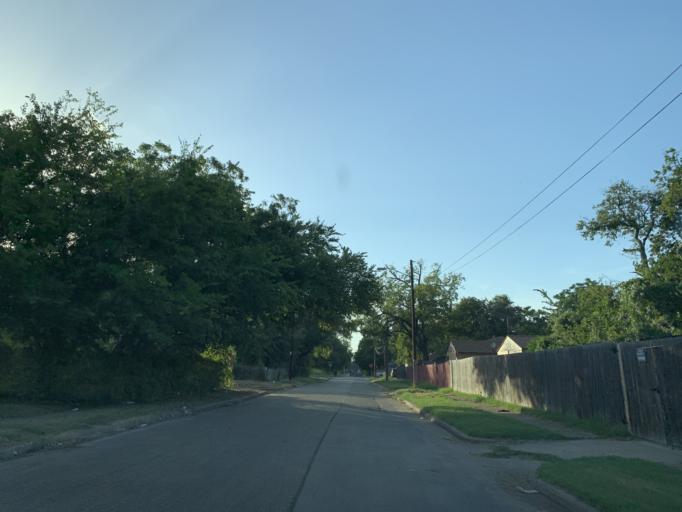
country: US
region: Texas
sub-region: Dallas County
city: Dallas
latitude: 32.7616
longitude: -96.7415
